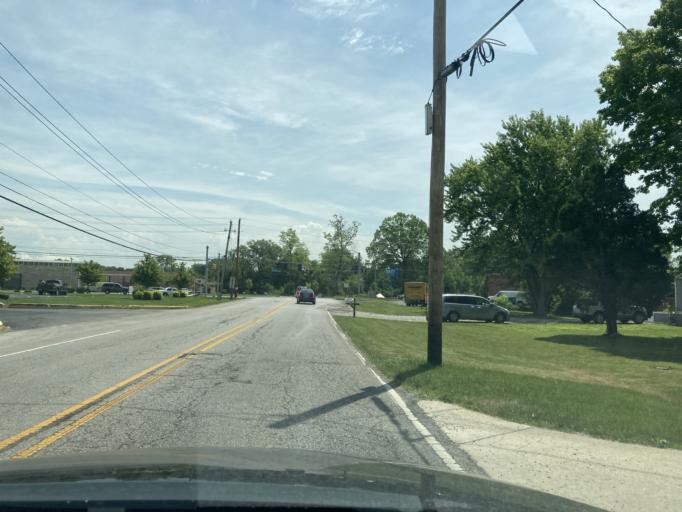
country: US
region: Indiana
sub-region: Marion County
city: Meridian Hills
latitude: 39.8680
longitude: -86.2031
